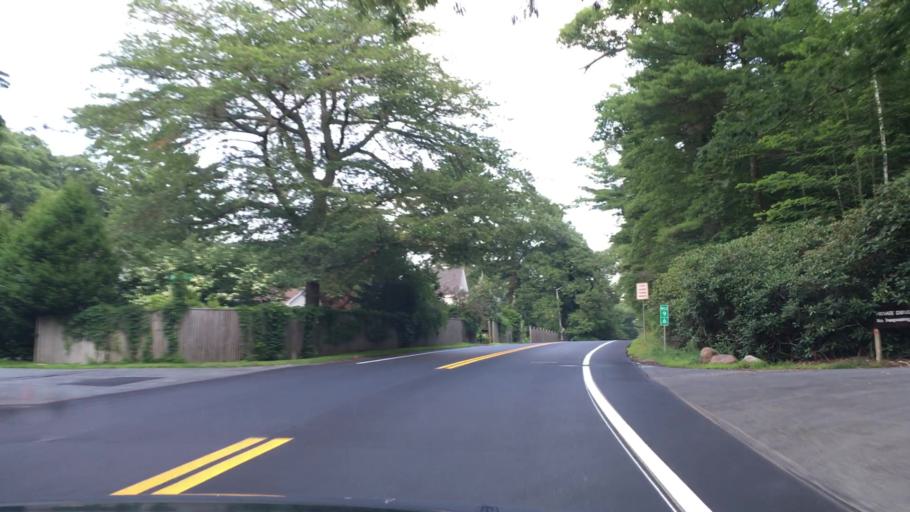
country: US
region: Massachusetts
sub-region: Essex County
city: Gloucester
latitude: 42.5800
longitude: -70.7279
